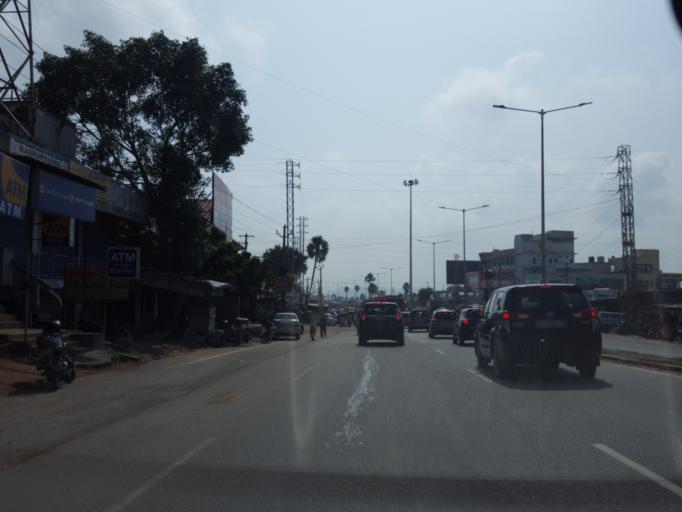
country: IN
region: Telangana
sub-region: Rangareddi
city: Lal Bahadur Nagar
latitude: 17.3105
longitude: 78.6855
